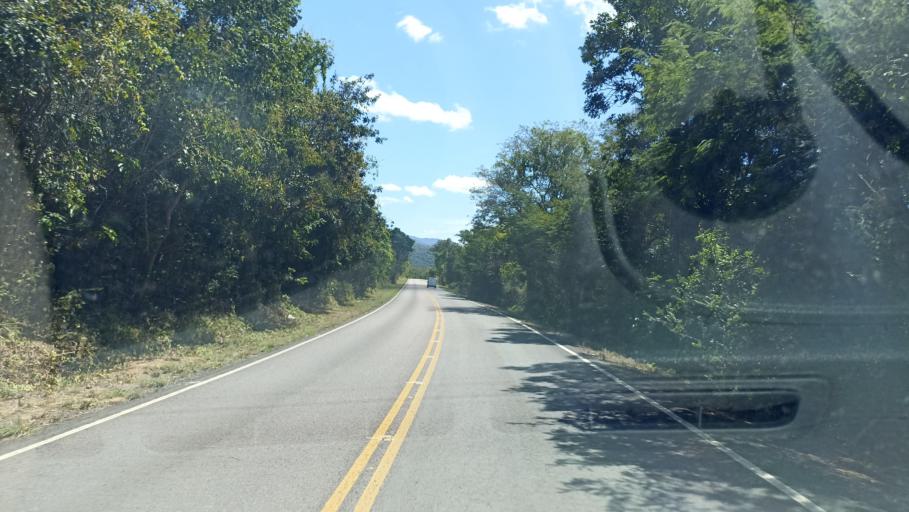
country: BR
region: Bahia
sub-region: Andarai
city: Vera Cruz
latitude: -12.7620
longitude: -41.3259
